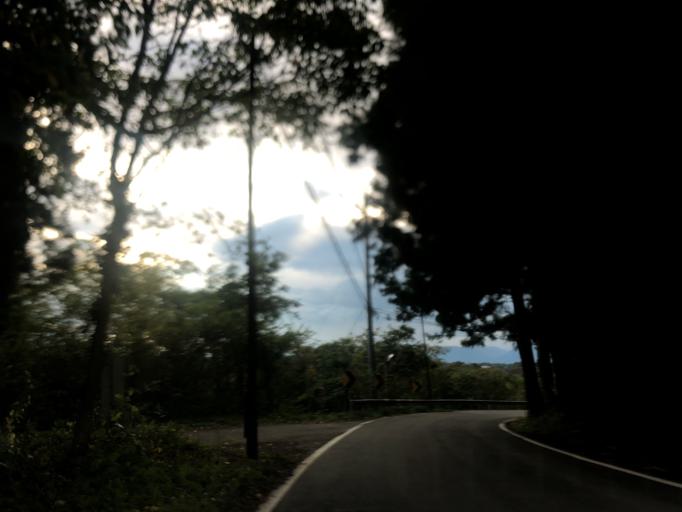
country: JP
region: Tochigi
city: Kuroiso
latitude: 36.9426
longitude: 140.1094
